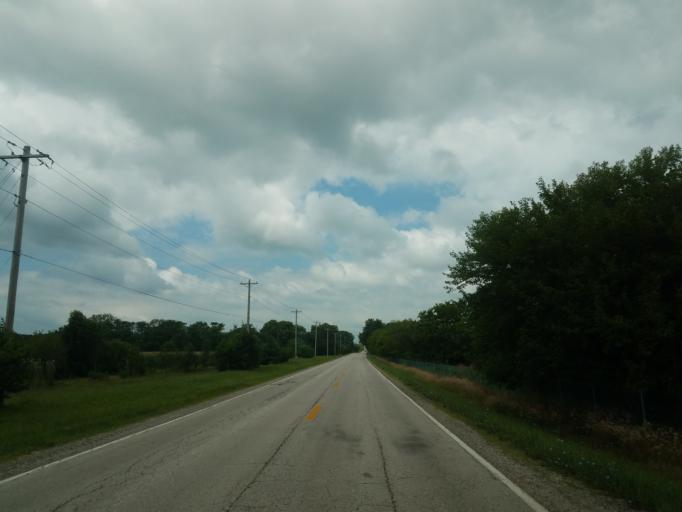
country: US
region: Illinois
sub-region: McLean County
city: Bloomington
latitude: 40.4586
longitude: -89.0377
